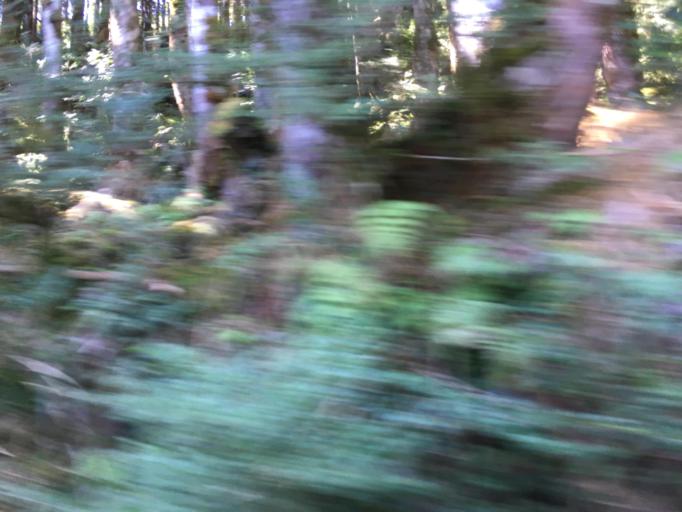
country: TW
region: Taiwan
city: Daxi
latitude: 24.5708
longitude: 121.4185
